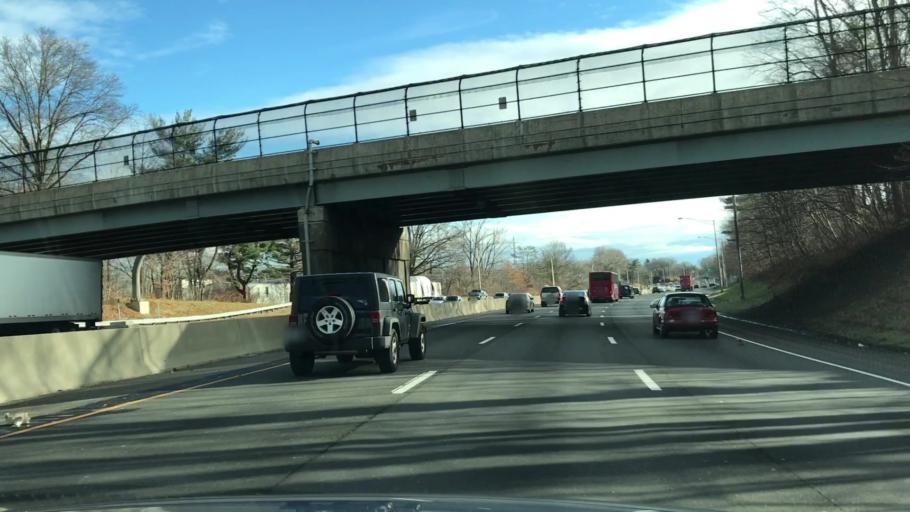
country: US
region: Connecticut
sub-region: Fairfield County
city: Darien
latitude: 41.0669
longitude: -73.4994
